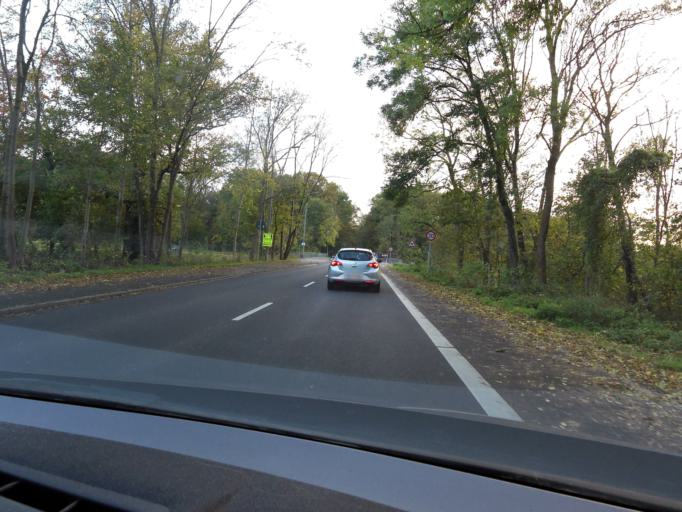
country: DE
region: Saxony
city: Leipzig
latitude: 51.3682
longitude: 12.3141
